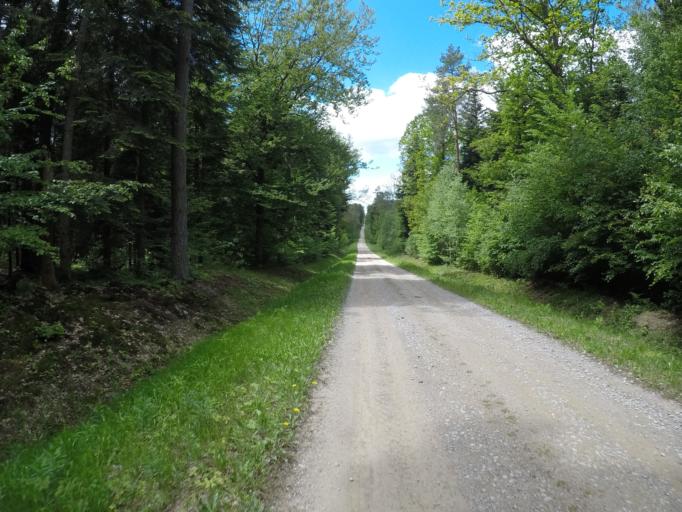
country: PL
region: Swietokrzyskie
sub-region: Powiat kielecki
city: Kostomloty Pierwsze
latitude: 50.9314
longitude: 20.6332
